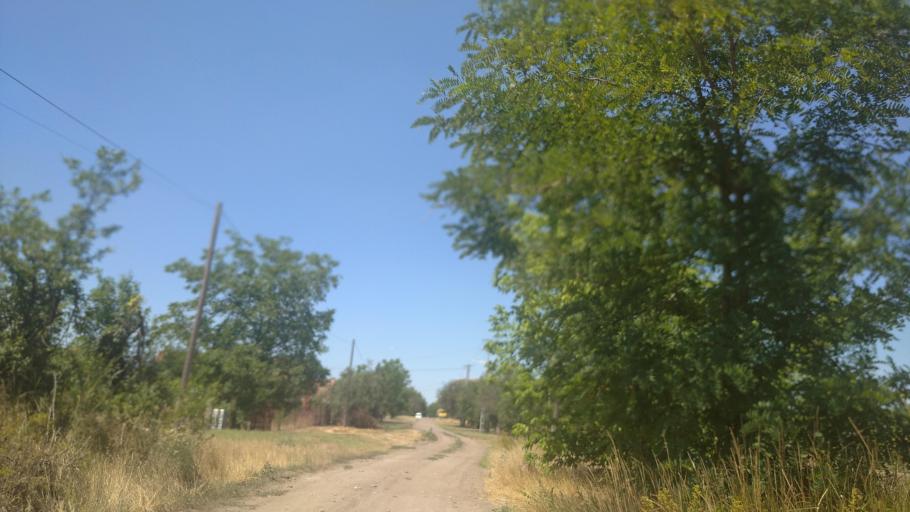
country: HU
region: Bekes
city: Oroshaza
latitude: 46.5574
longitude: 20.6208
